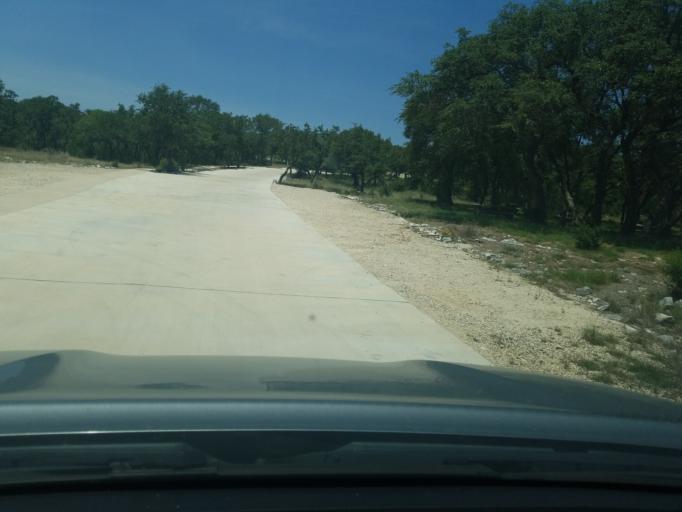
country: US
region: Texas
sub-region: Bexar County
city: Timberwood Park
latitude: 29.6835
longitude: -98.4562
